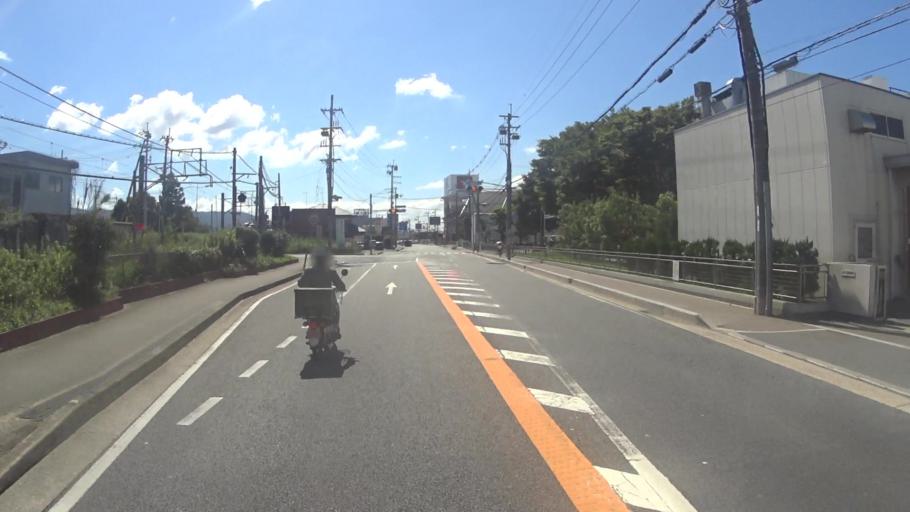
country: JP
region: Kyoto
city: Tanabe
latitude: 34.8450
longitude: 135.7861
